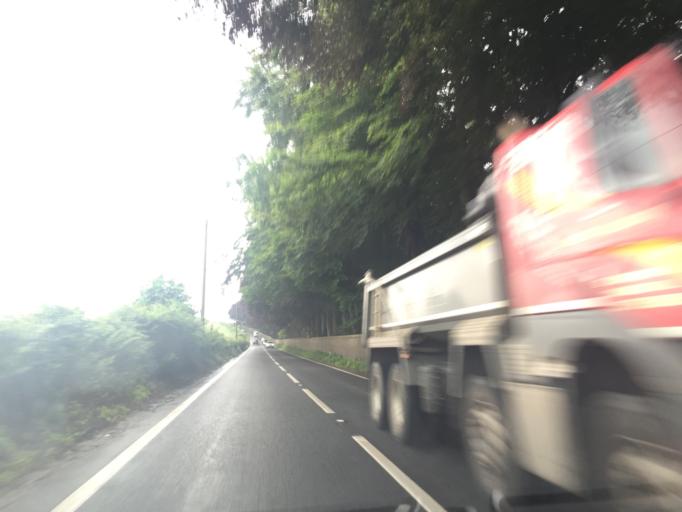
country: GB
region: England
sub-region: Dorset
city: Lytchett Matravers
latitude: 50.7894
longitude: -2.0914
